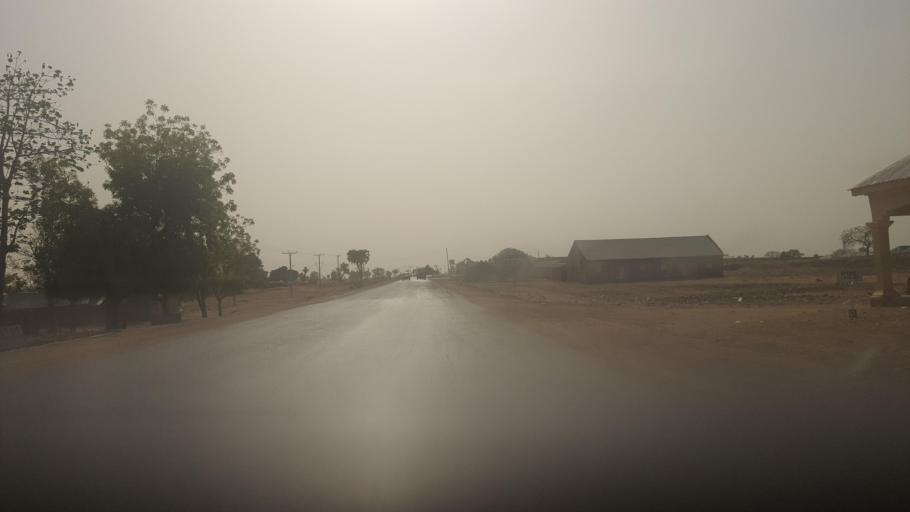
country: NG
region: Bauchi
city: Bauchi
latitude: 10.2613
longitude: 9.9931
